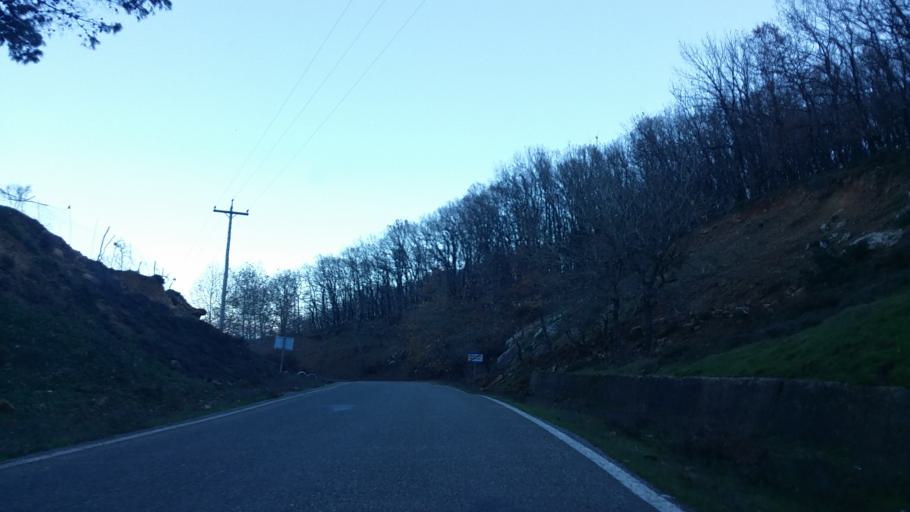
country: GR
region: West Greece
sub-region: Nomos Aitolias kai Akarnanias
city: Sardinia
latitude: 38.8653
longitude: 21.2958
